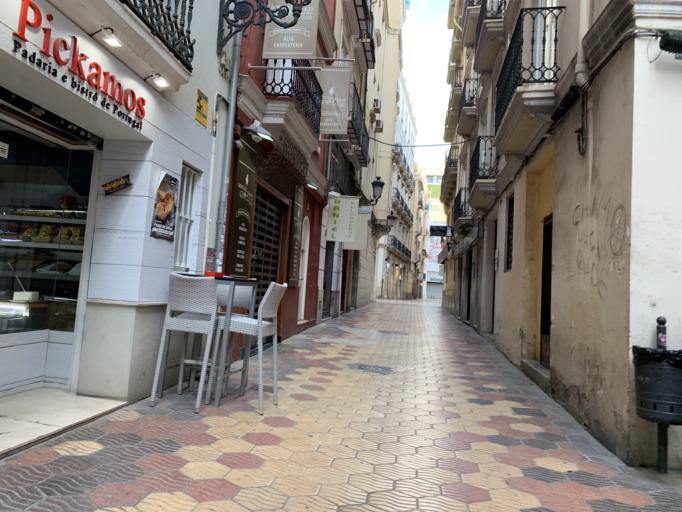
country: ES
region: Valencia
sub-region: Provincia de Valencia
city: Valencia
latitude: 39.4706
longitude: -0.3726
